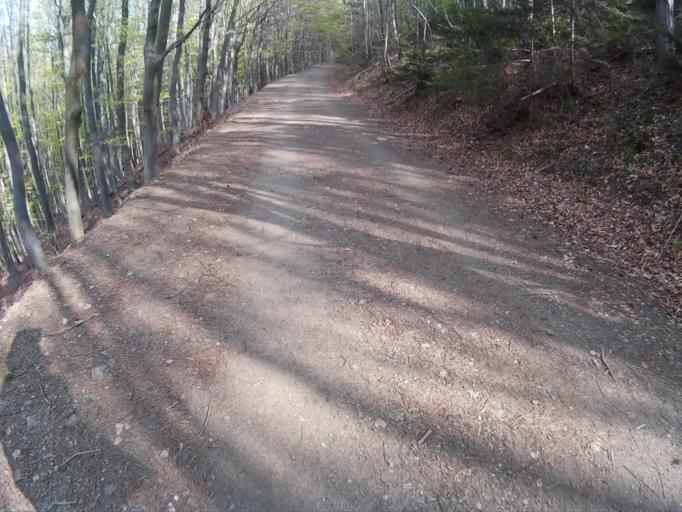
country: AT
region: Burgenland
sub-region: Politischer Bezirk Oberwart
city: Rechnitz
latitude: 47.3397
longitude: 16.4572
